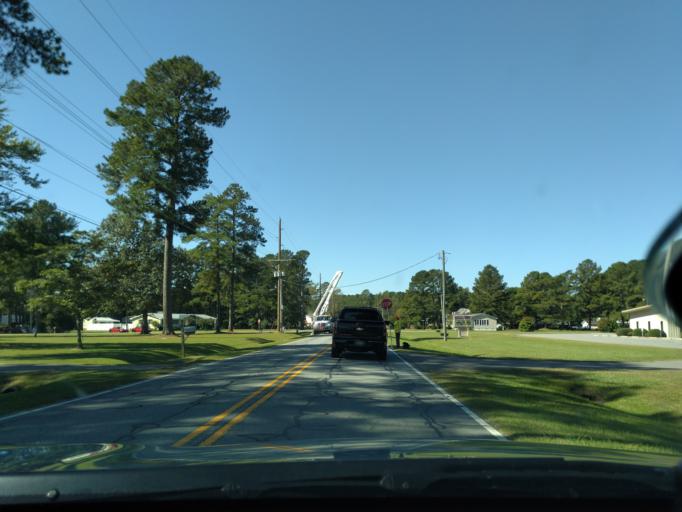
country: US
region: North Carolina
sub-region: Beaufort County
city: Washington
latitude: 35.5607
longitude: -77.0005
